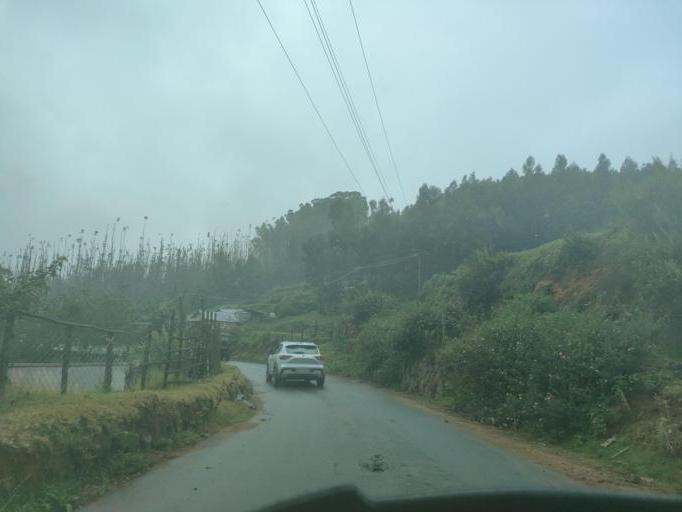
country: IN
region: Tamil Nadu
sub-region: Dindigul
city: Kodaikanal
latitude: 10.2341
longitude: 77.3497
